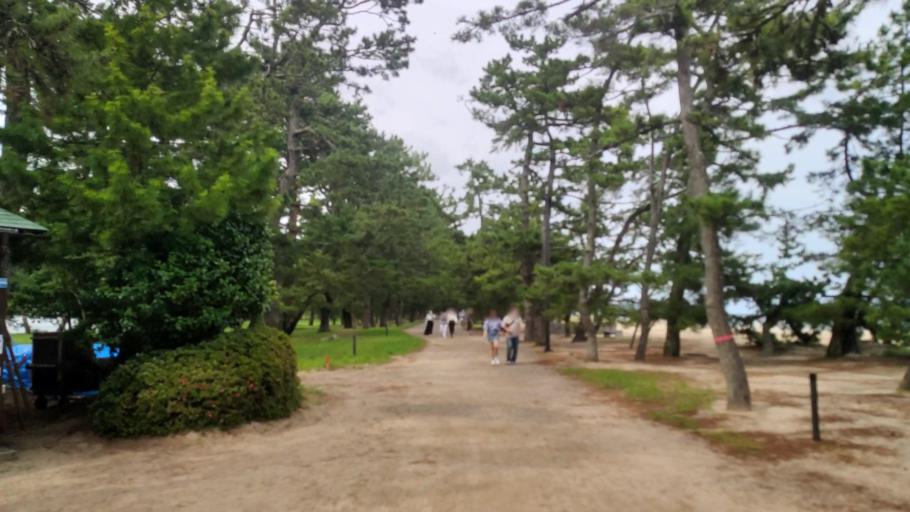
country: JP
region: Kyoto
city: Miyazu
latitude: 35.5594
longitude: 135.1870
